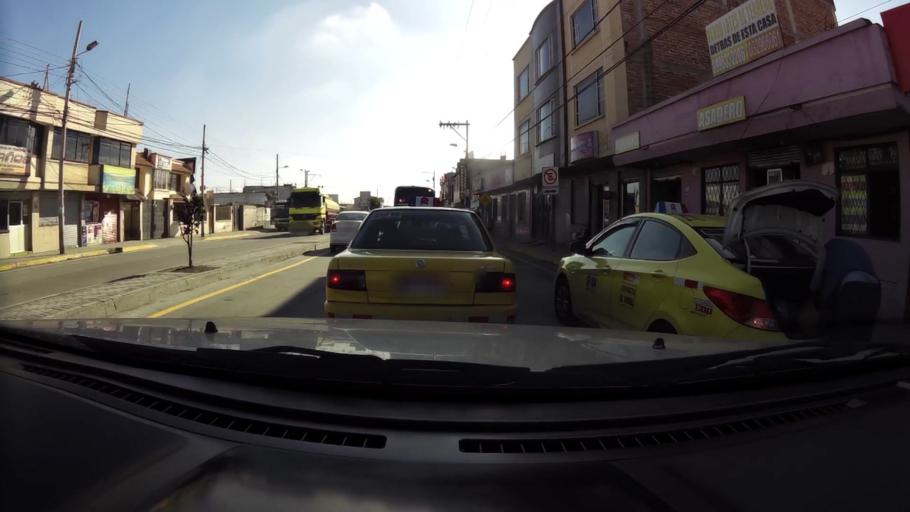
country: EC
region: Chimborazo
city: Riobamba
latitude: -1.6453
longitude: -78.6746
